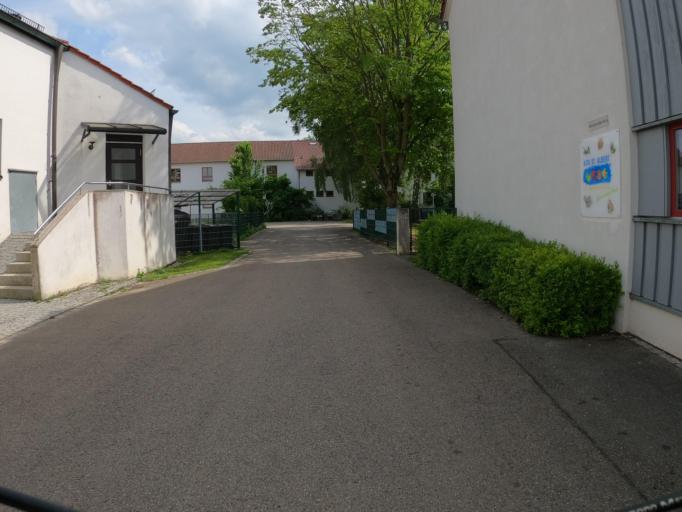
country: DE
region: Bavaria
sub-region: Swabia
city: Neu-Ulm
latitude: 48.4010
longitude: 10.0198
